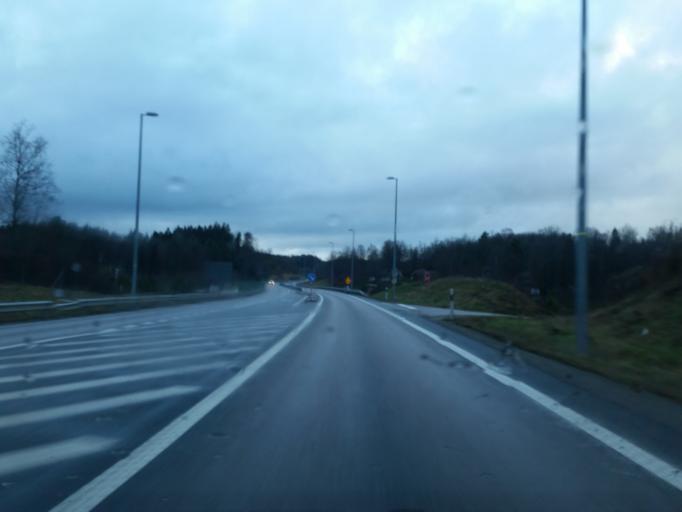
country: SE
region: Vaestra Goetaland
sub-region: Boras Kommun
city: Boras
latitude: 57.6804
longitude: 12.9635
